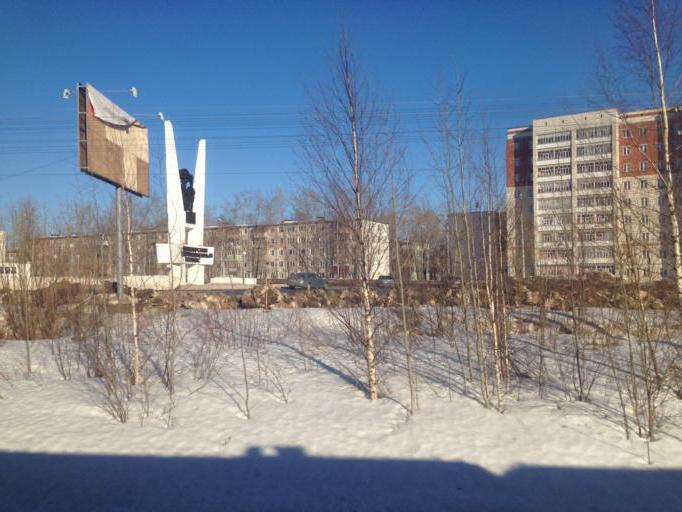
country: RU
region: Komi Republic
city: Ezhva
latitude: 61.7963
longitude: 50.7375
